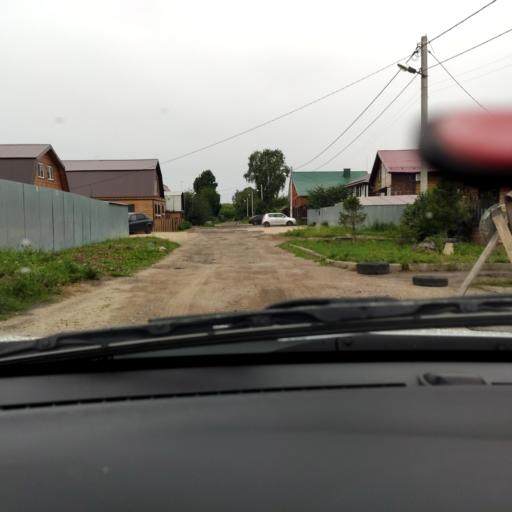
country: RU
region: Tatarstan
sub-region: Gorod Kazan'
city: Kazan
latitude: 55.8440
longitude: 49.1985
